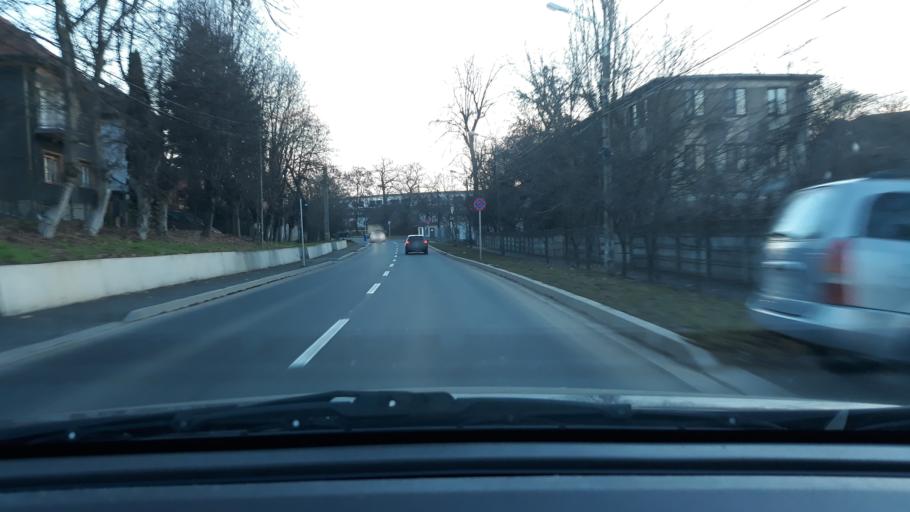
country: RO
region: Bihor
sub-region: Comuna Biharea
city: Oradea
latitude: 47.0833
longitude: 21.9273
